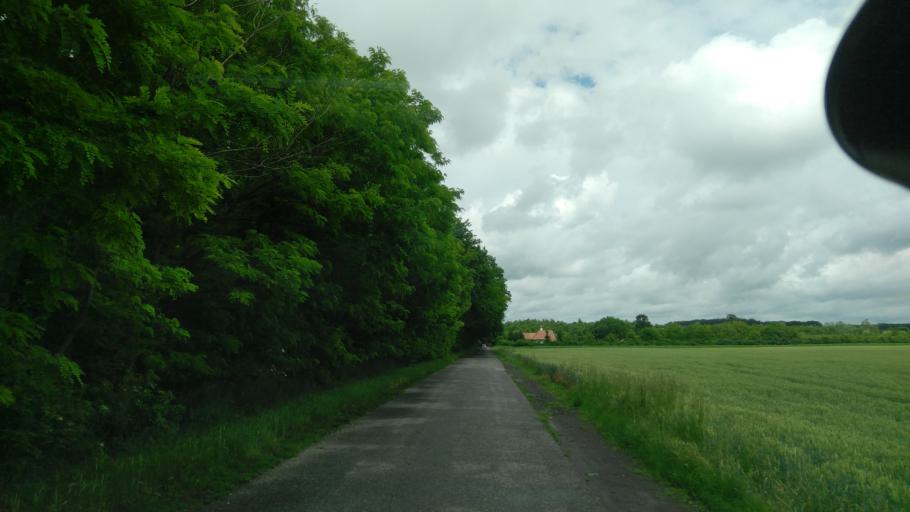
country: HU
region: Bekes
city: Doboz
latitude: 46.6794
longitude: 21.1886
